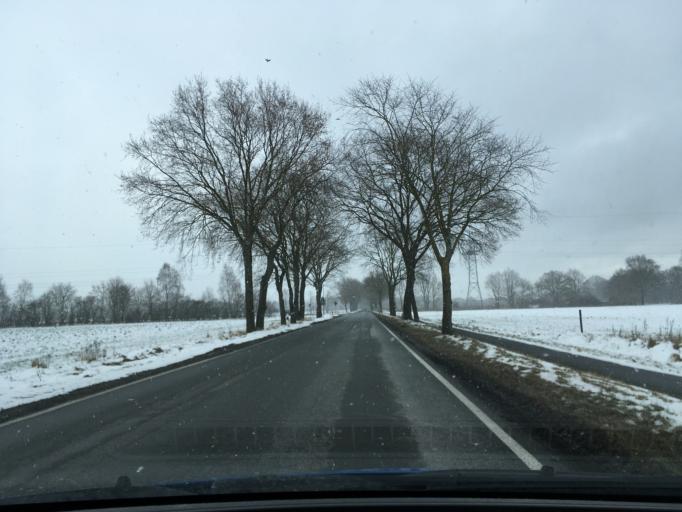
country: DE
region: Lower Saxony
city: Winsen
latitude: 53.3275
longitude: 10.2125
